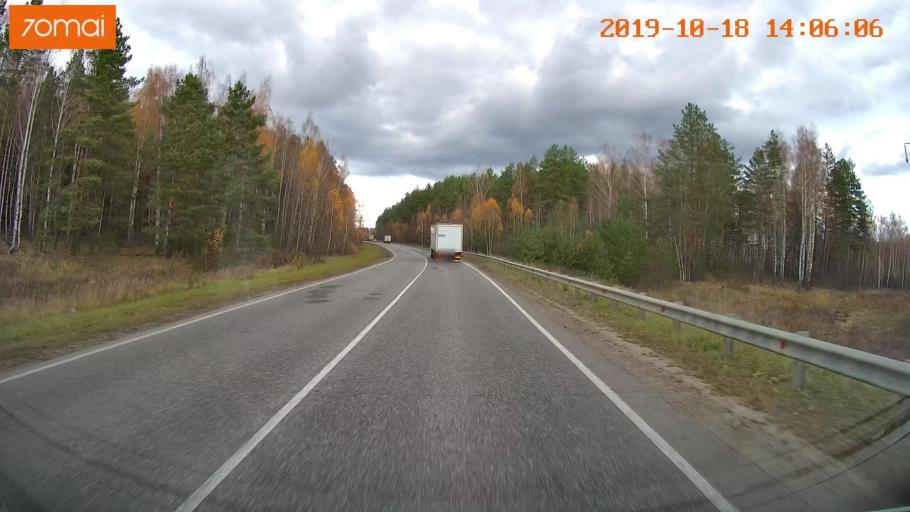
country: RU
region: Rjazan
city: Spas-Klepiki
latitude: 55.1412
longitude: 40.1486
